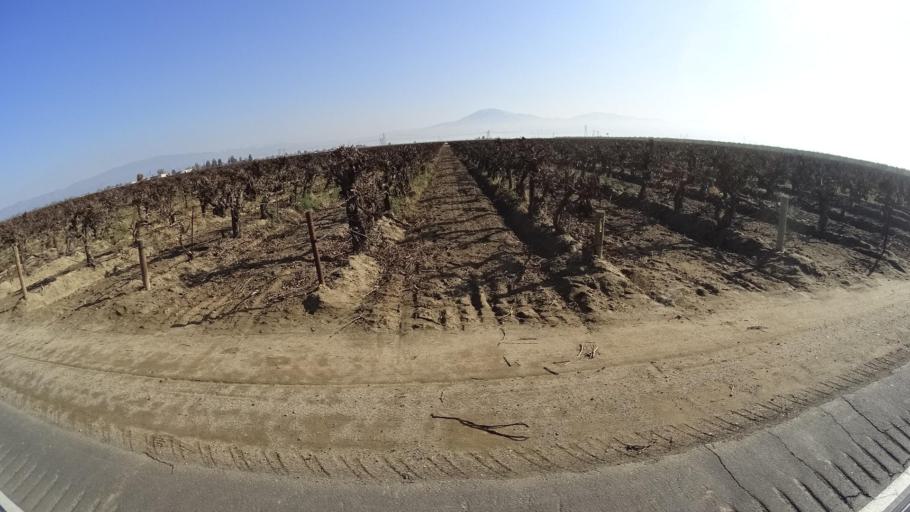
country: US
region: California
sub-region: Kern County
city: Weedpatch
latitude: 35.2322
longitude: -118.9322
